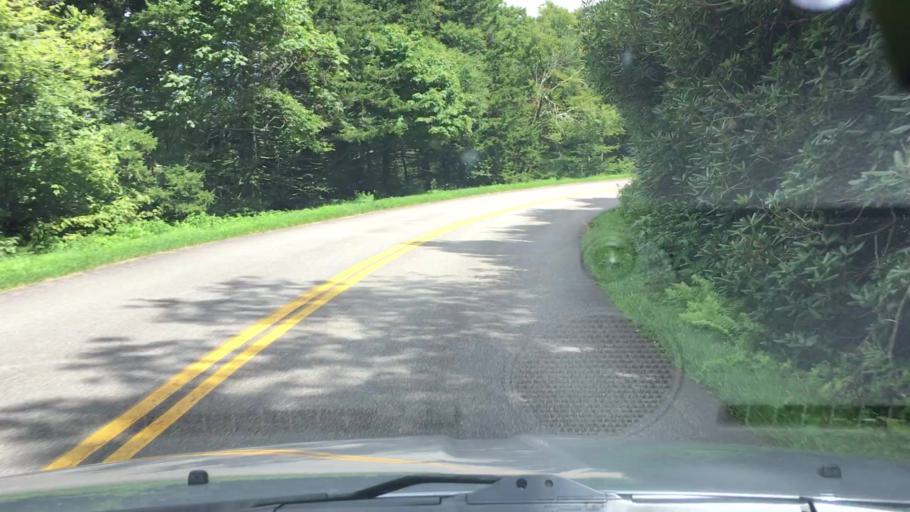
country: US
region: North Carolina
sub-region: Buncombe County
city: Black Mountain
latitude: 35.7084
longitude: -82.2642
